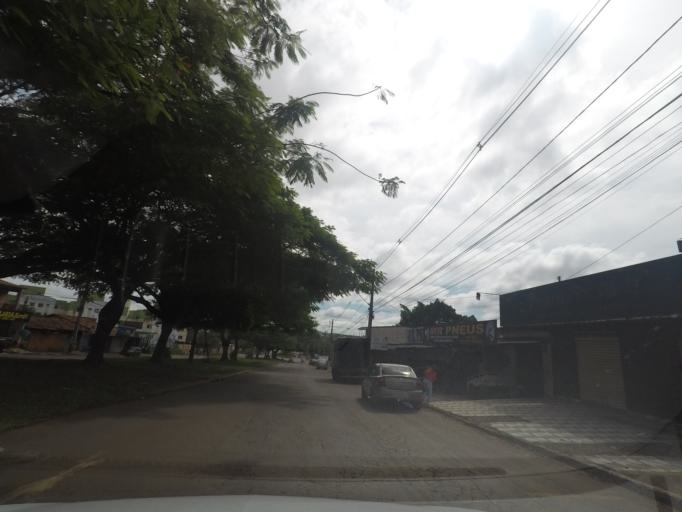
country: BR
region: Goias
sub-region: Goiania
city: Goiania
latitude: -16.6614
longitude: -49.2118
